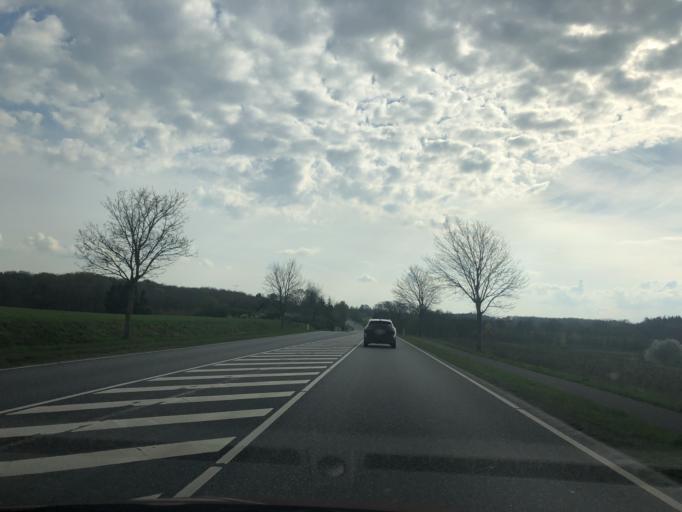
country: DK
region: Zealand
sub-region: Lejre Kommune
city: Osted
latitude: 55.5327
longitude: 11.9176
